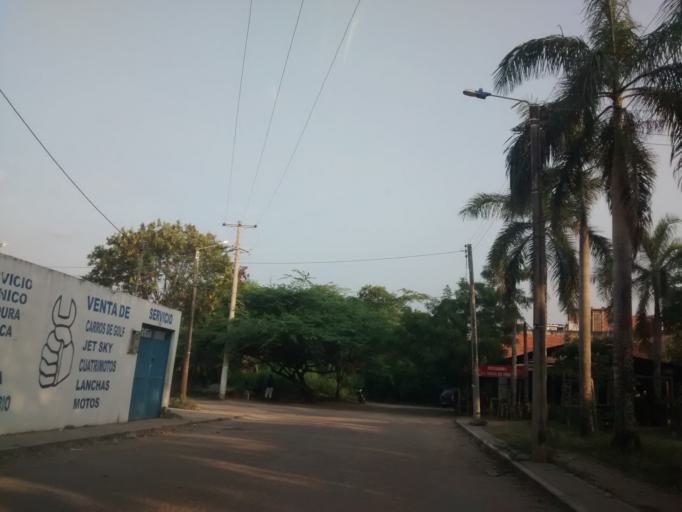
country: CO
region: Cundinamarca
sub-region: Girardot
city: Girardot City
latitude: 4.3157
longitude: -74.7817
